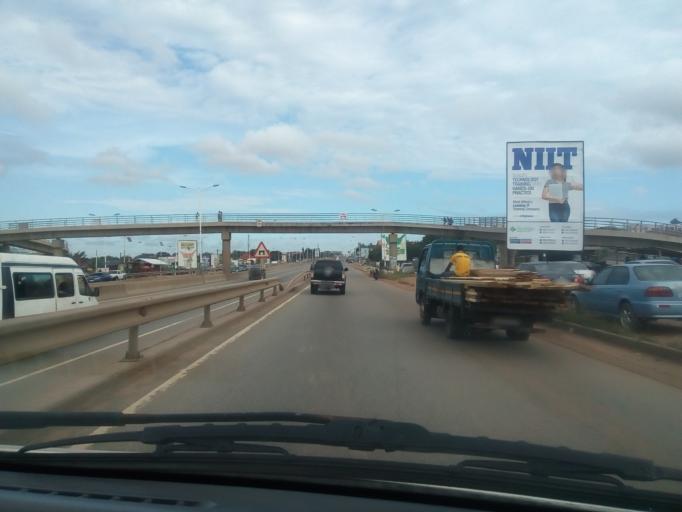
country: GH
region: Greater Accra
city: Dome
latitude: 5.6500
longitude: -0.2539
